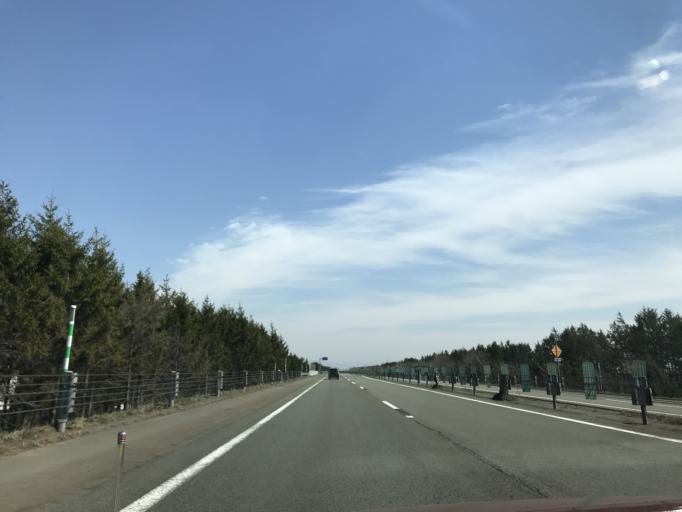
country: JP
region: Hokkaido
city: Ebetsu
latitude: 43.1245
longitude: 141.6376
